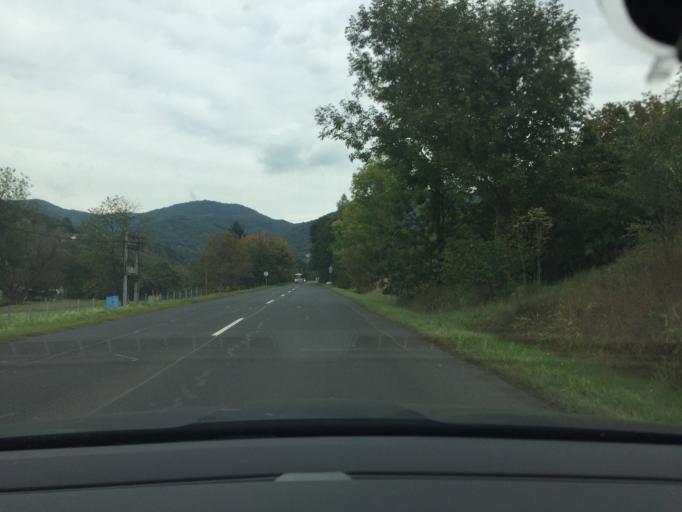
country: CZ
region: Ustecky
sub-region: Okres Usti nad Labem
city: Usti nad Labem
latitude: 50.5939
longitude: 14.0482
